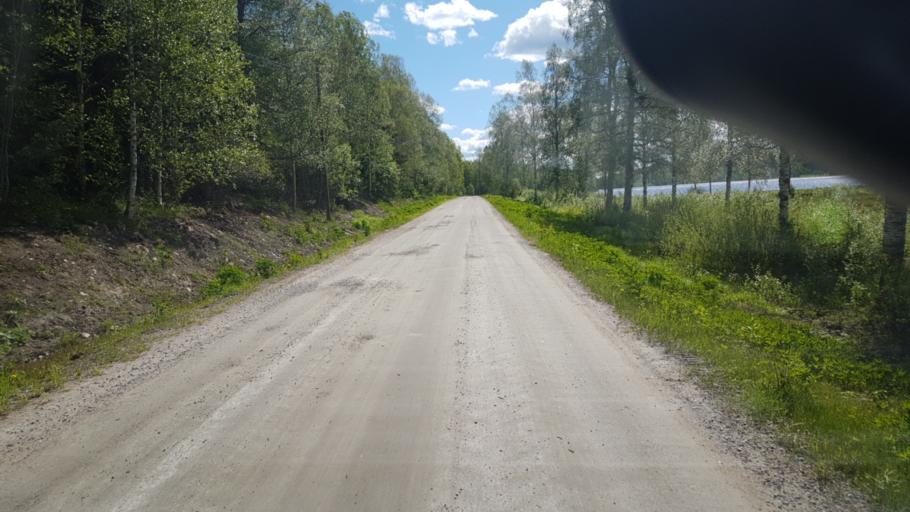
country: SE
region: Vaermland
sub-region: Arvika Kommun
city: Arvika
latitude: 59.7476
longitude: 12.8299
